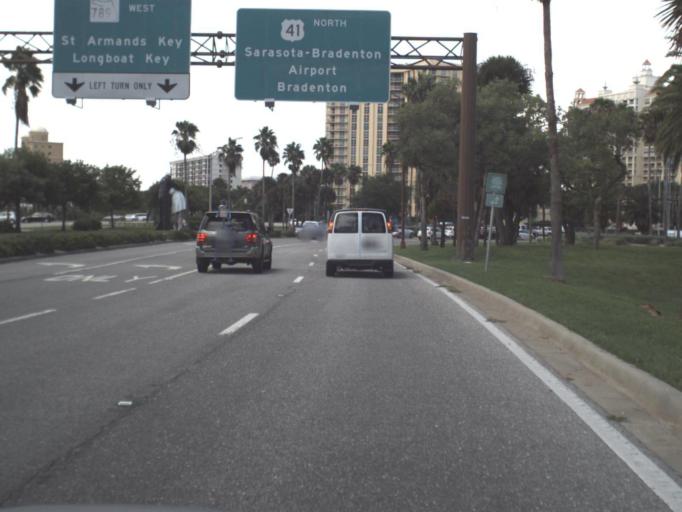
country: US
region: Florida
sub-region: Sarasota County
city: Sarasota
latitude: 27.3349
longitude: -82.5455
